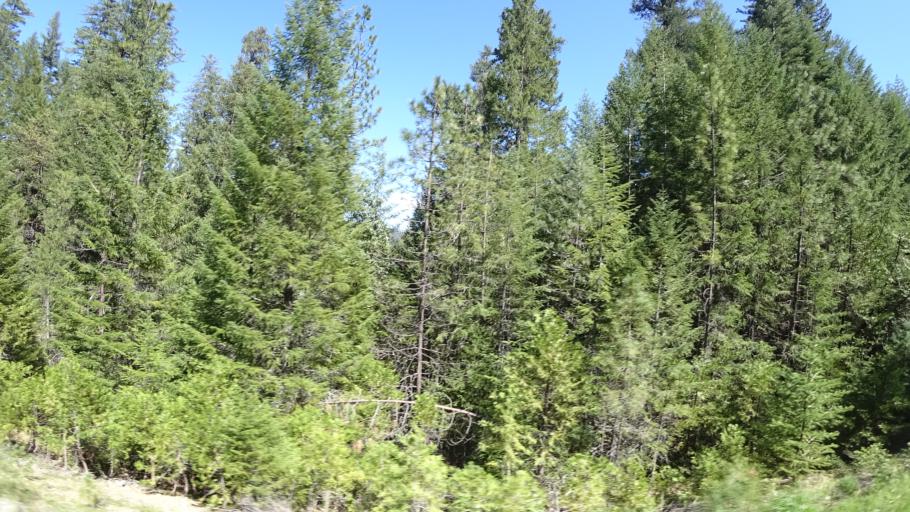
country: US
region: California
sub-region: Trinity County
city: Lewiston
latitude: 40.9040
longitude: -122.7885
